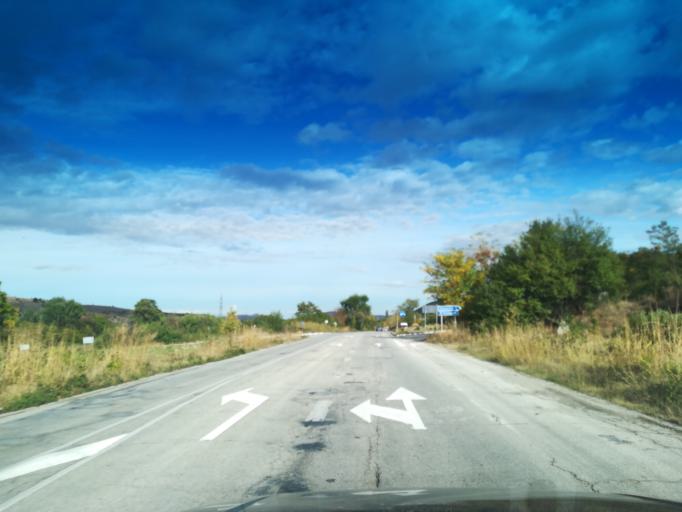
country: BG
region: Pazardzhik
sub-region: Obshtina Bratsigovo
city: Bratsigovo
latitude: 42.0620
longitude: 24.3540
